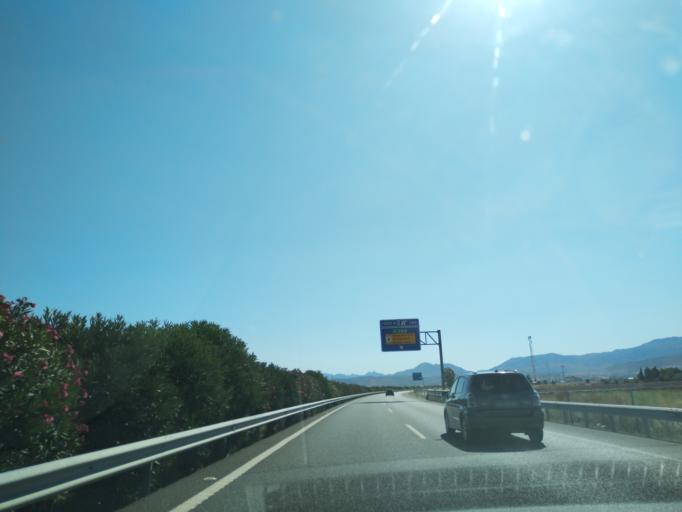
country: ES
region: Andalusia
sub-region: Provincia de Malaga
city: Mollina
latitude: 37.0818
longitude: -4.6160
